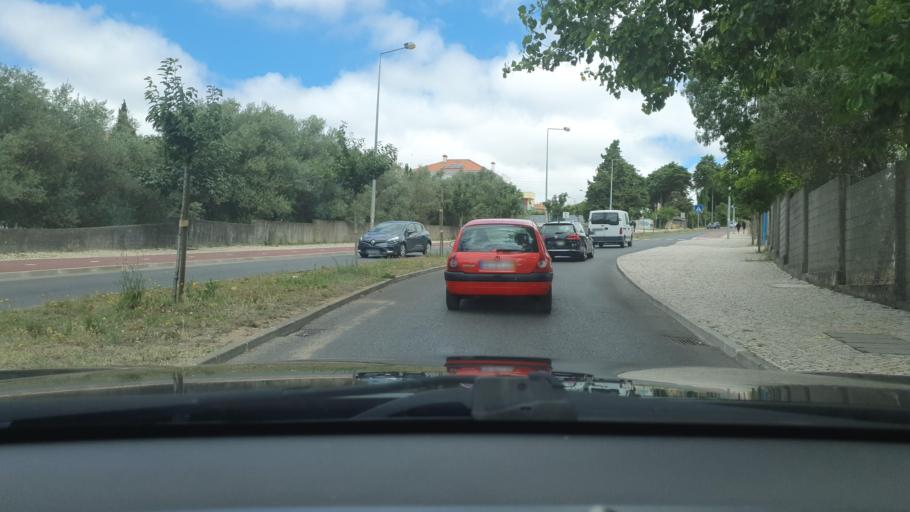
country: PT
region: Lisbon
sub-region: Sintra
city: Cacem
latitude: 38.7588
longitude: -9.2783
